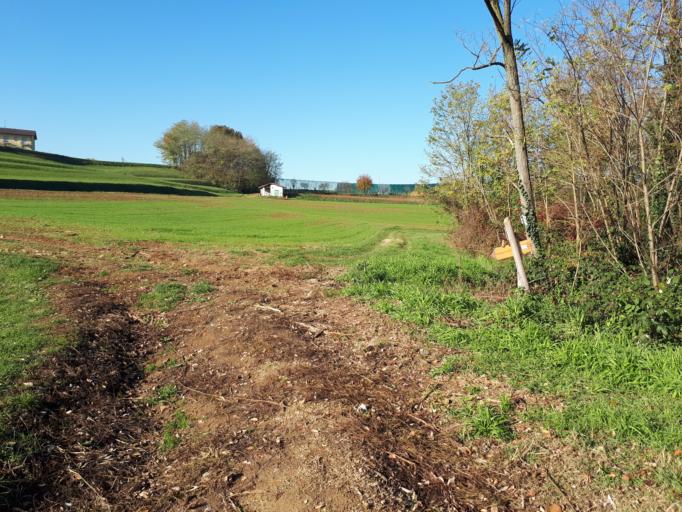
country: IT
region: Lombardy
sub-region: Provincia di Lecco
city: Maresso
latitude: 45.6967
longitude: 9.3599
